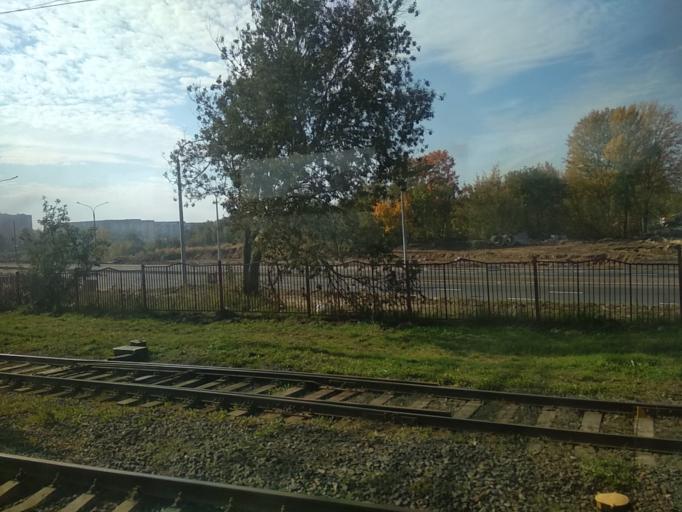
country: BY
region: Minsk
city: Syenitsa
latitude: 53.8596
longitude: 27.5588
